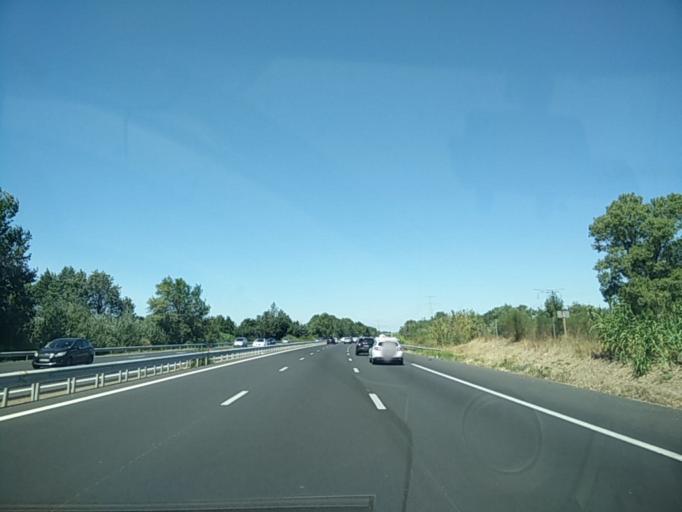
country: FR
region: Provence-Alpes-Cote d'Azur
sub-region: Departement du Vaucluse
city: Cavaillon
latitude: 43.8420
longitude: 4.9933
